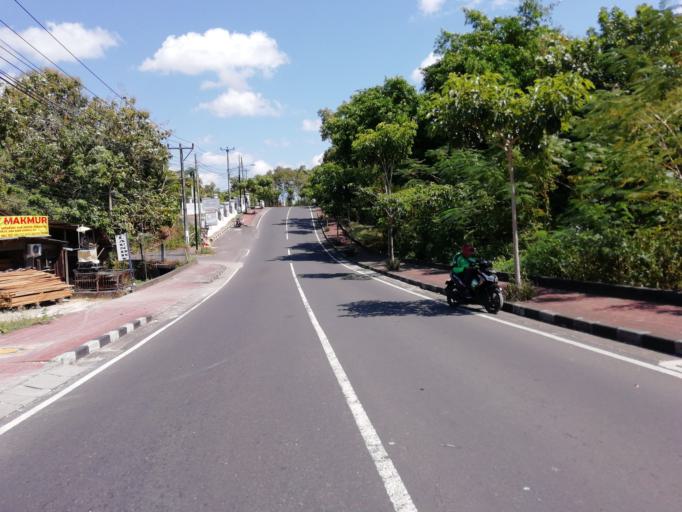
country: ID
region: Bali
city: Jimbaran
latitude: -8.7976
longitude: 115.1742
